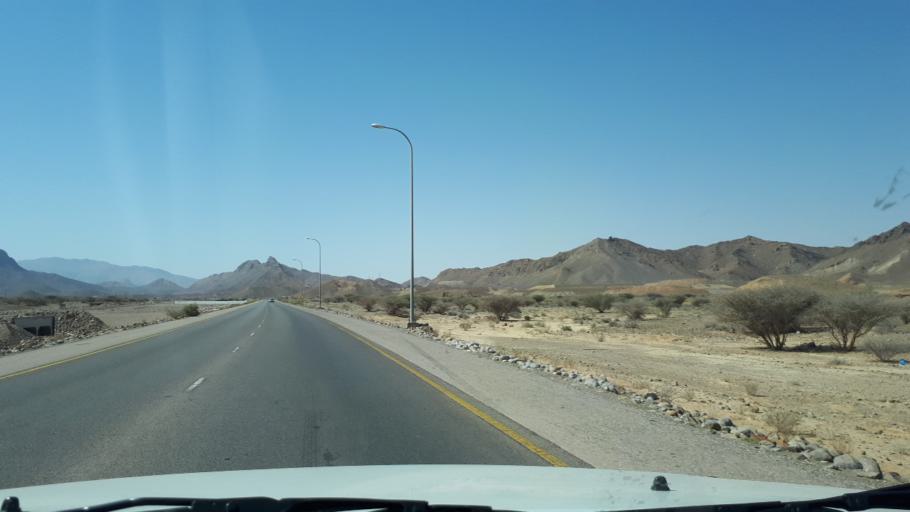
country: OM
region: Ash Sharqiyah
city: Sur
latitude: 22.3609
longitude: 59.3123
